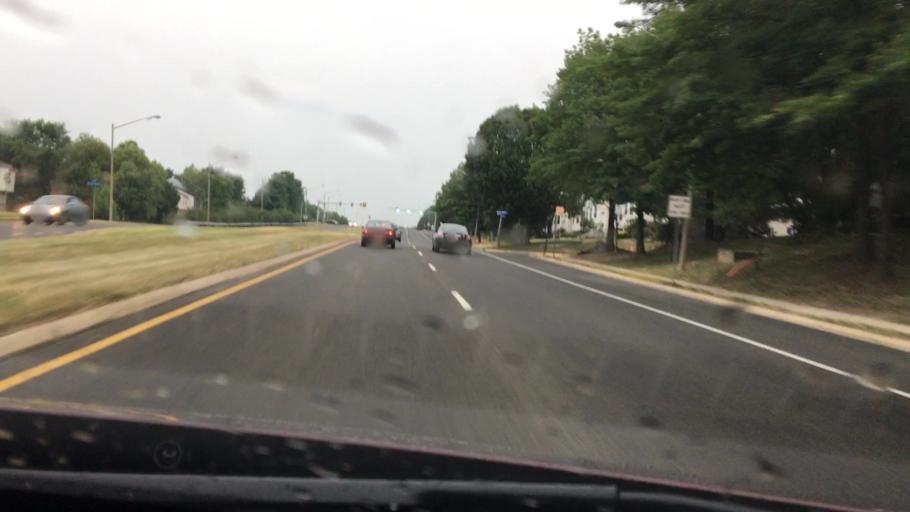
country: US
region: Virginia
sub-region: Fairfax County
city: Centreville
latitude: 38.8284
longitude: -77.4277
